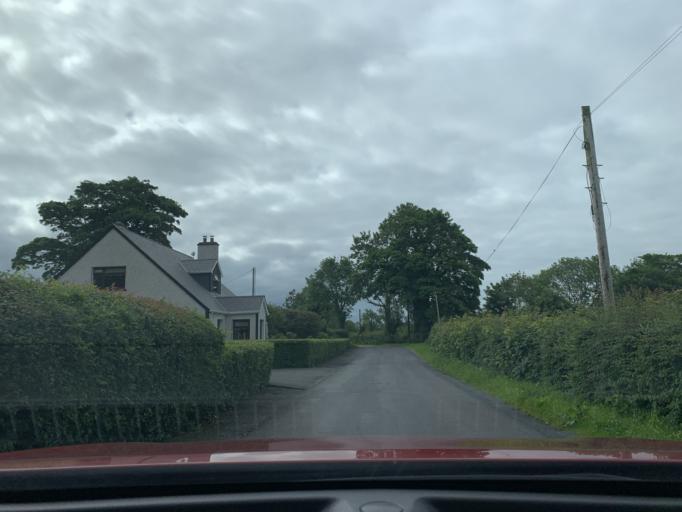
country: IE
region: Connaught
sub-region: Sligo
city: Sligo
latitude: 54.3373
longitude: -8.4743
